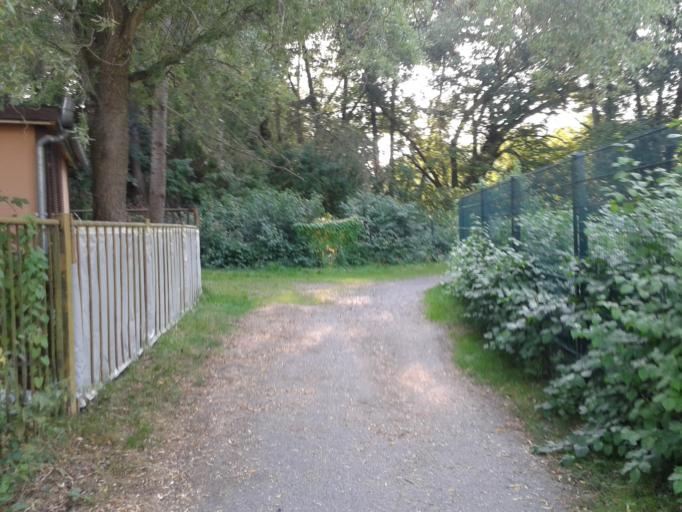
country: DE
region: Saxony
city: Dresden
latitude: 51.0156
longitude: 13.7471
